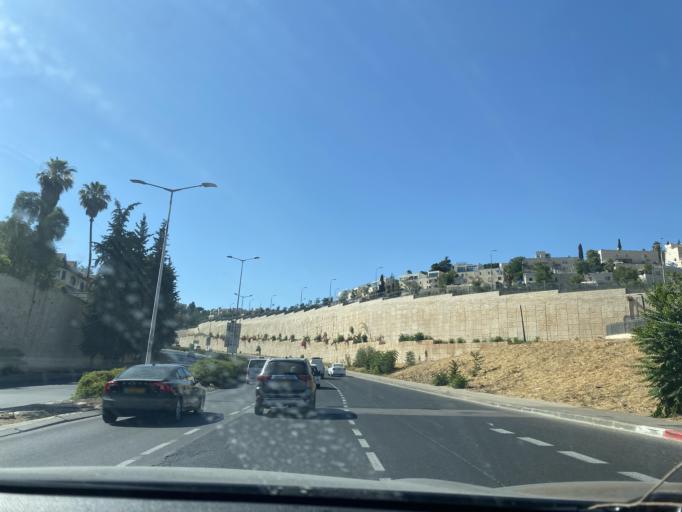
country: PS
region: West Bank
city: Bayt Iksa
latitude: 31.8103
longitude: 35.2038
